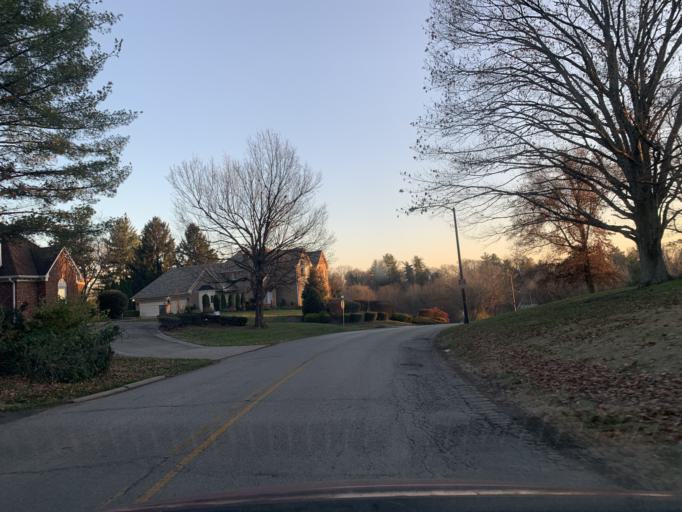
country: US
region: Kentucky
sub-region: Jefferson County
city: Saint Matthews
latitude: 38.2449
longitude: -85.6875
